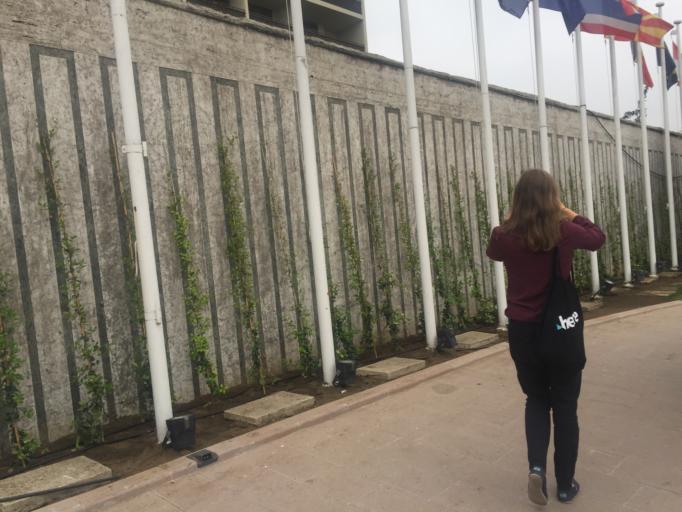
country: TR
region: Istanbul
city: Sisli
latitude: 41.0444
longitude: 28.9889
